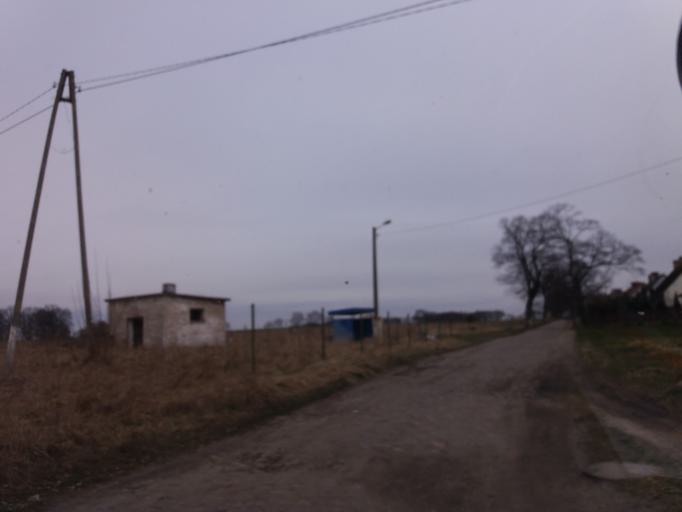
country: PL
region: West Pomeranian Voivodeship
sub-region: Powiat choszczenski
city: Recz
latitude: 53.1586
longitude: 15.6086
